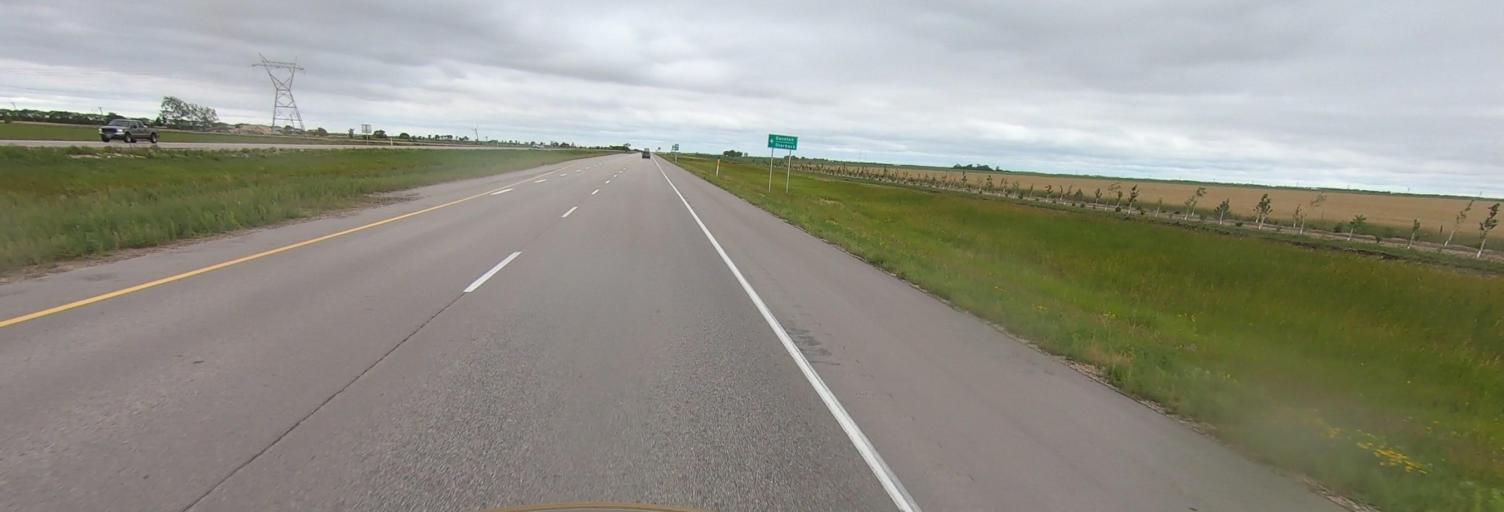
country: CA
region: Manitoba
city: Headingley
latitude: 49.8871
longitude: -97.6361
